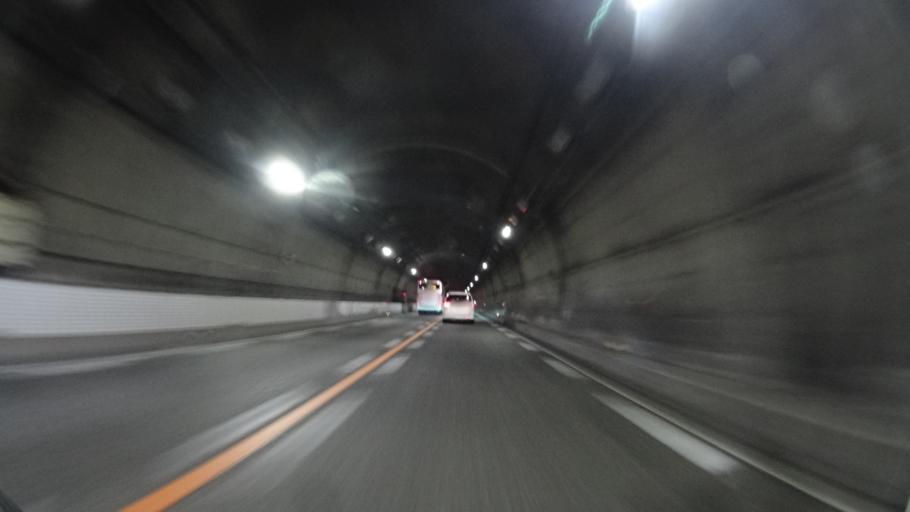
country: JP
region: Okayama
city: Okayama-shi
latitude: 34.7108
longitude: 133.9164
